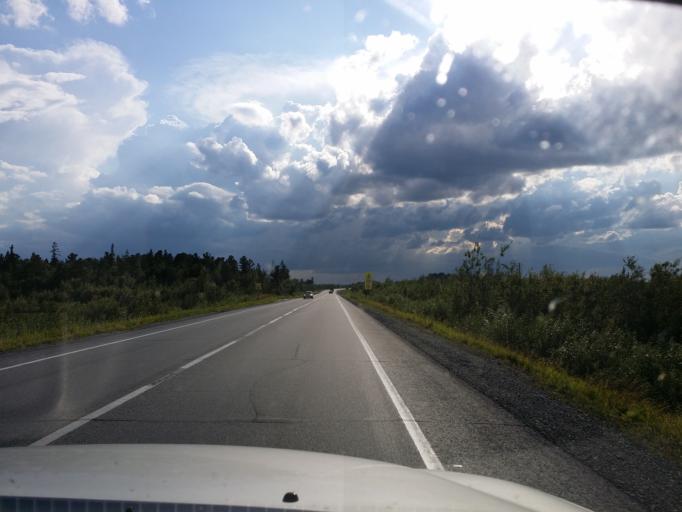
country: RU
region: Khanty-Mansiyskiy Avtonomnyy Okrug
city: Surgut
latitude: 61.4536
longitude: 74.0555
